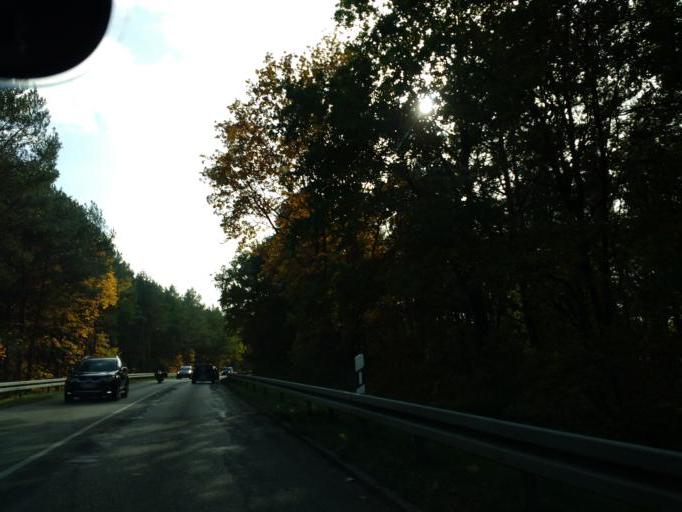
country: DE
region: Brandenburg
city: Petershagen
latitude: 52.5311
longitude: 13.8189
